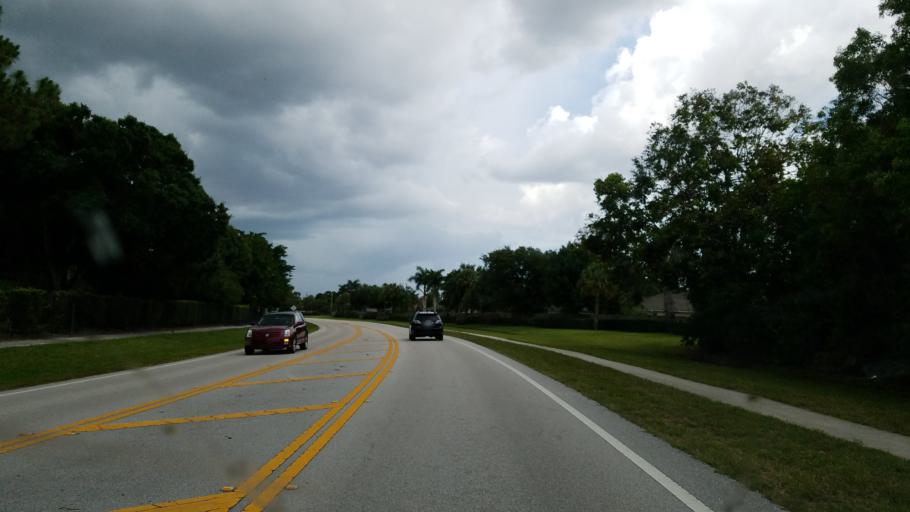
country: US
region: Florida
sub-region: Martin County
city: Palm City
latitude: 27.1652
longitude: -80.2946
